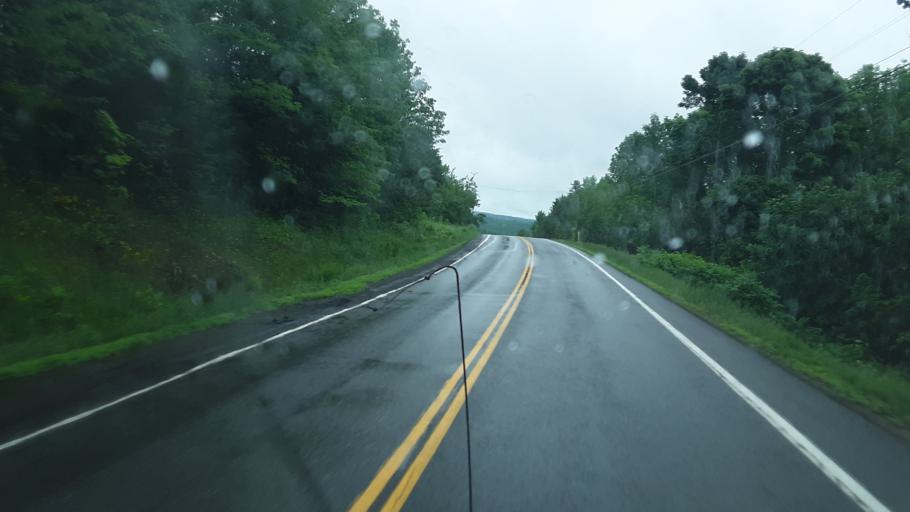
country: US
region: Maine
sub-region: Penobscot County
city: Patten
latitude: 46.0828
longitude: -68.4307
